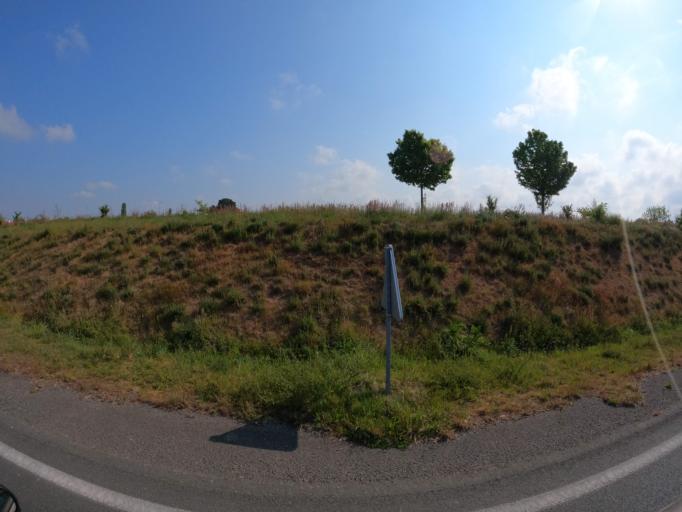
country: FR
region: Pays de la Loire
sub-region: Departement de la Vendee
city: La Bruffiere
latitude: 47.0091
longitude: -1.2006
